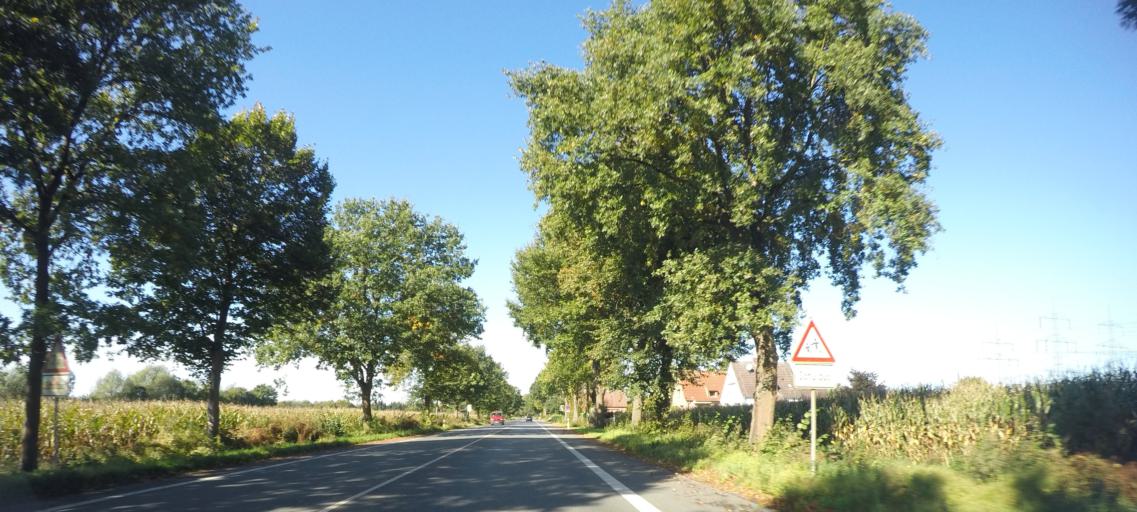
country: DE
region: North Rhine-Westphalia
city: Ahlen
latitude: 51.7007
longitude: 7.9262
